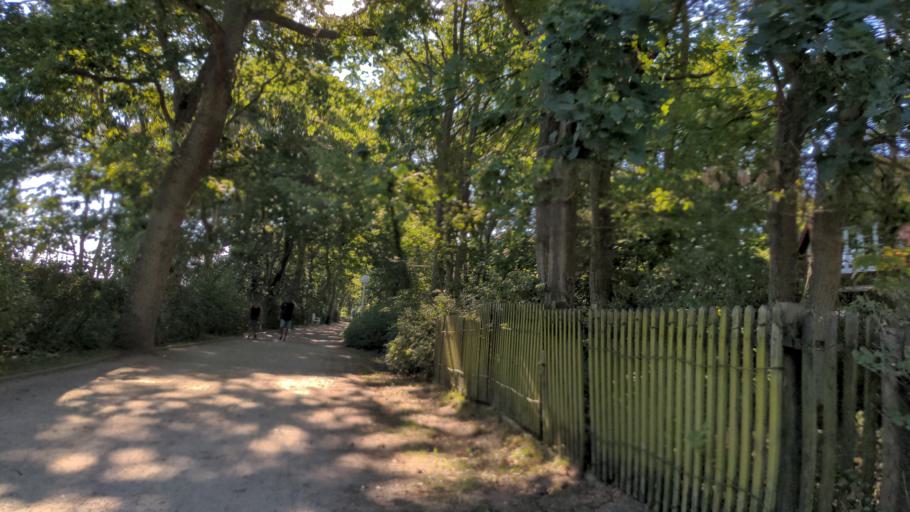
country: DE
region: Mecklenburg-Vorpommern
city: Ostseebad Boltenhagen
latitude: 53.9821
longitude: 11.2253
